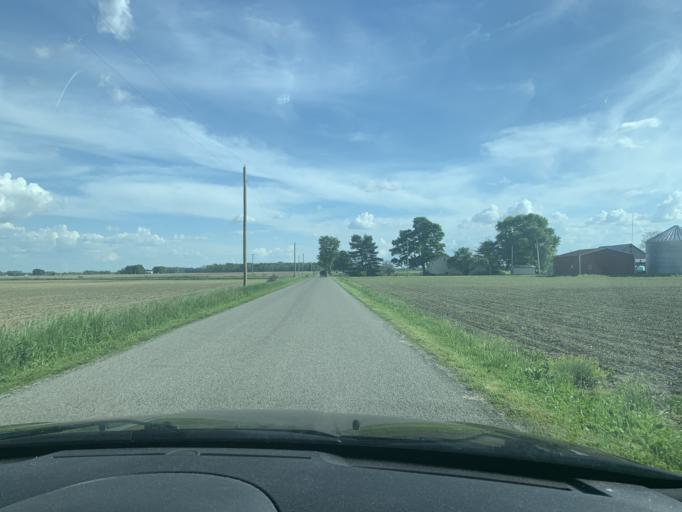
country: US
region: Ohio
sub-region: Logan County
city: De Graff
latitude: 40.2531
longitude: -84.0167
